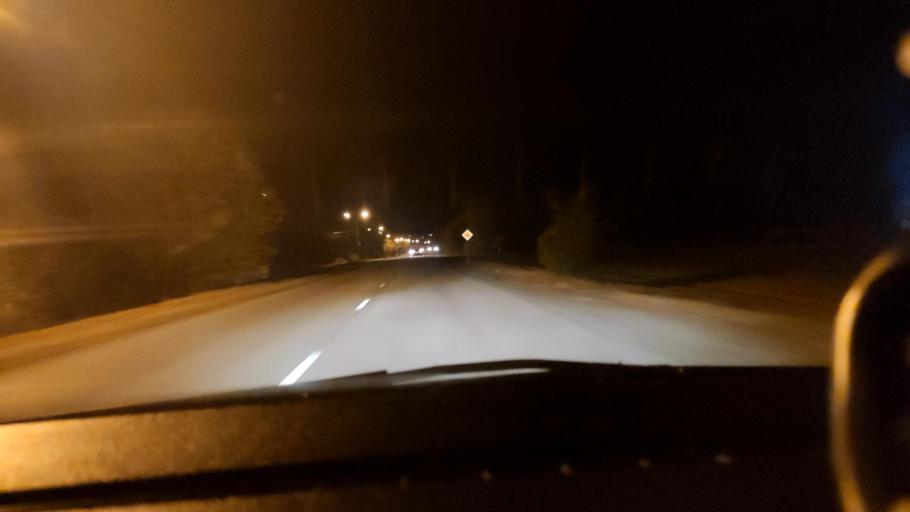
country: RU
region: Voronezj
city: Shilovo
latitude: 51.5585
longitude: 39.1068
